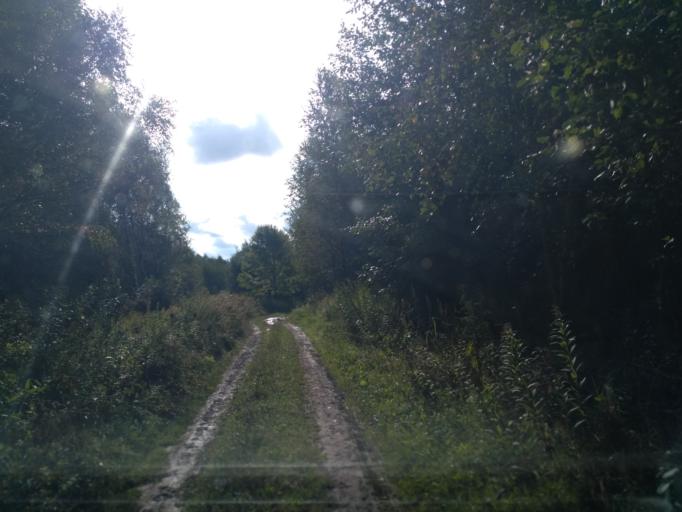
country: PL
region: Subcarpathian Voivodeship
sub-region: Powiat strzyzowski
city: Jawornik
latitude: 49.8479
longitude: 21.8568
